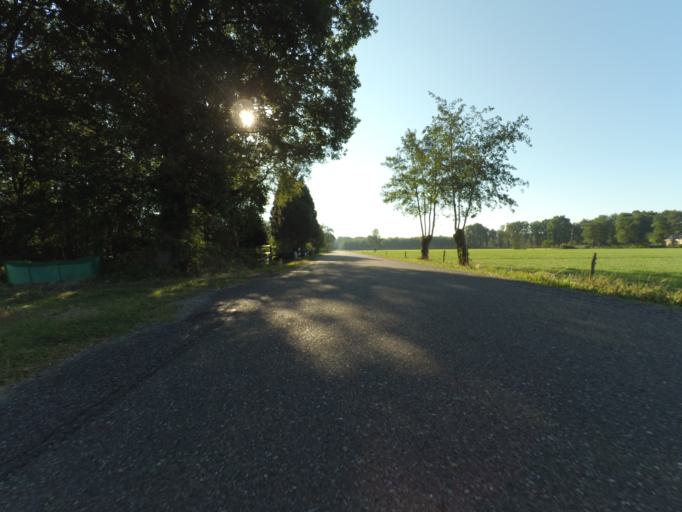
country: NL
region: Gelderland
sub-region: Gemeente Barneveld
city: Voorthuizen
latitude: 52.1951
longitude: 5.5607
